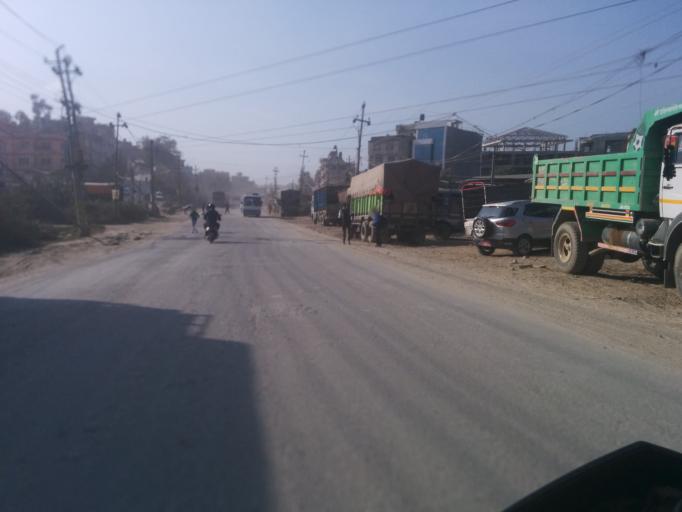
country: NP
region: Central Region
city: Kirtipur
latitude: 27.6882
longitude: 85.2878
